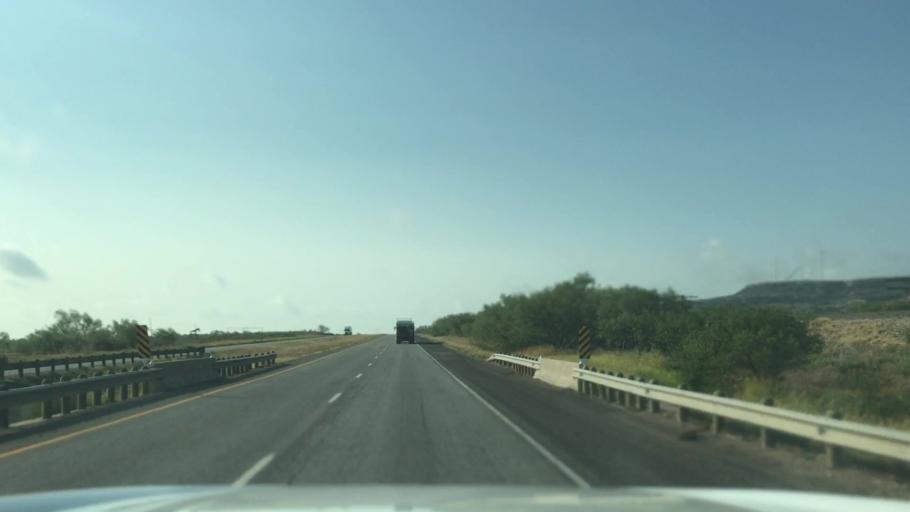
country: US
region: Texas
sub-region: Scurry County
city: Snyder
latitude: 32.9719
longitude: -101.0999
